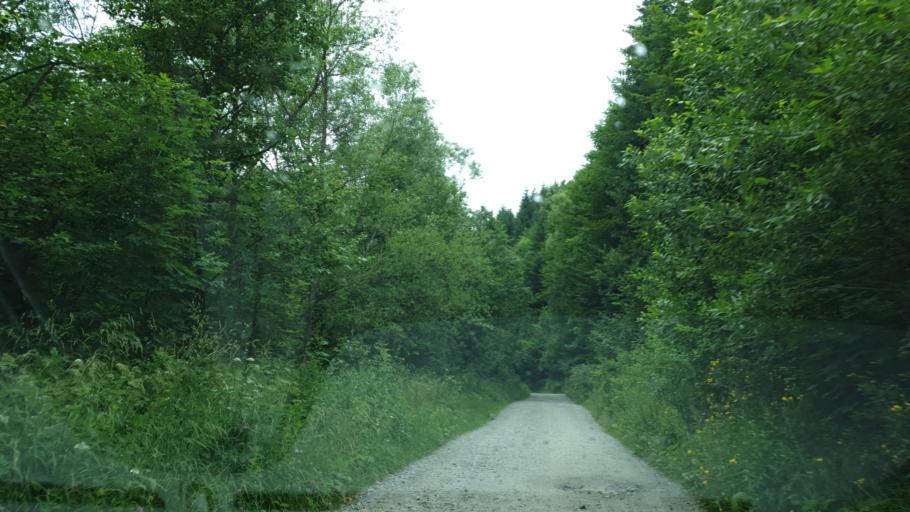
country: RO
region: Hunedoara
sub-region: Comuna Uricani
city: Uricani
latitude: 45.3001
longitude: 22.9928
